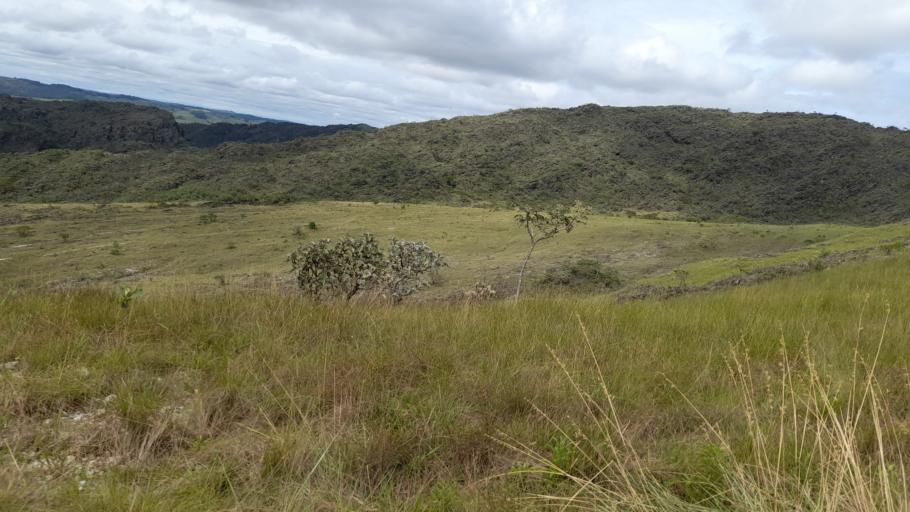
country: BR
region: Minas Gerais
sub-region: Sao Joao Del Rei
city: Sao Joao del Rei
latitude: -21.1181
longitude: -44.2821
